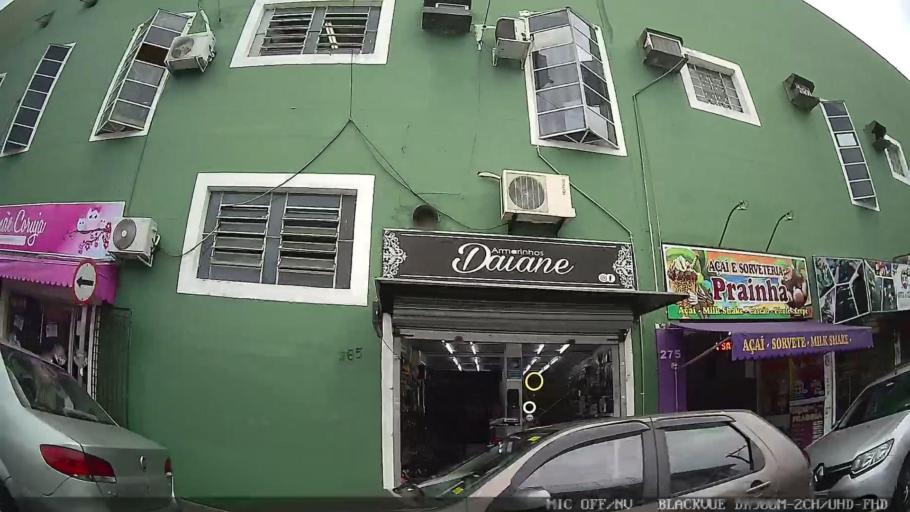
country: BR
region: Sao Paulo
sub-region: Caraguatatuba
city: Caraguatatuba
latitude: -23.6214
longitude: -45.4108
